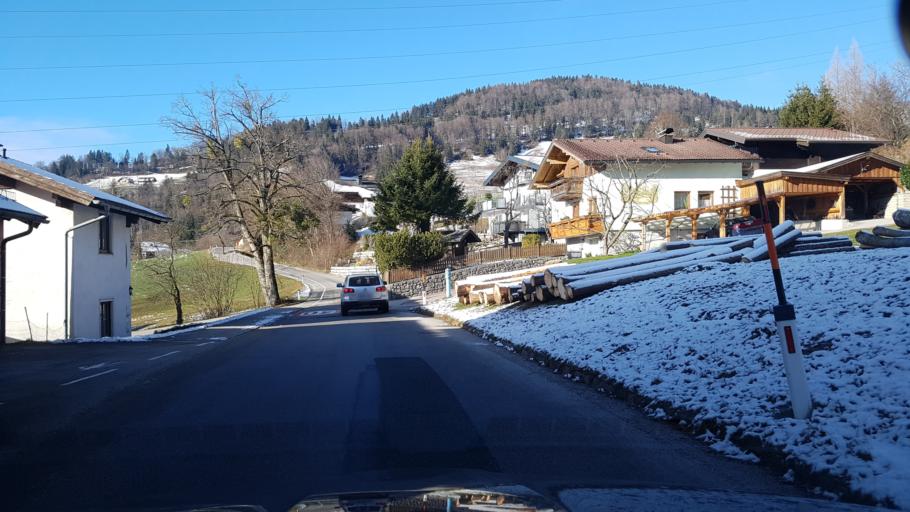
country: AT
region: Salzburg
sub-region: Politischer Bezirk Salzburg-Umgebung
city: Koppl
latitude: 47.7749
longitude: 13.1254
